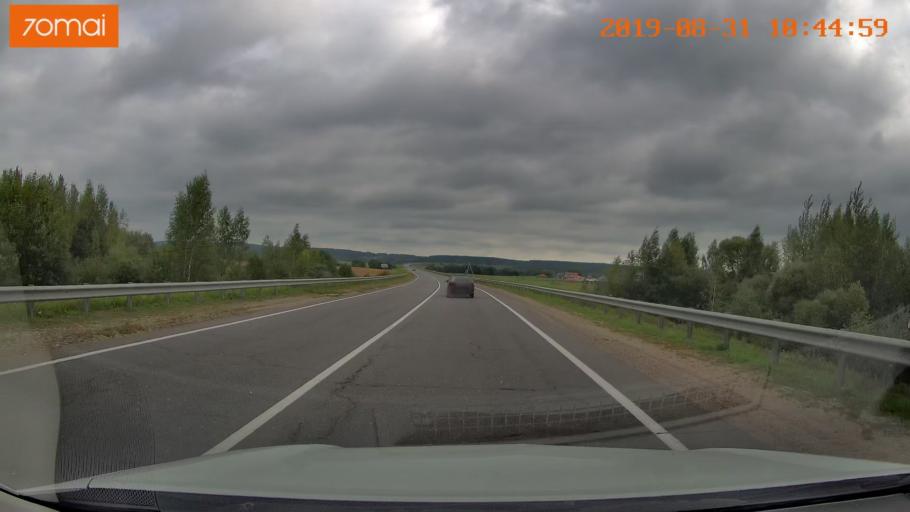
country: BY
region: Mogilev
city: Palykavichy Pyershyya
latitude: 53.9728
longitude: 30.3723
